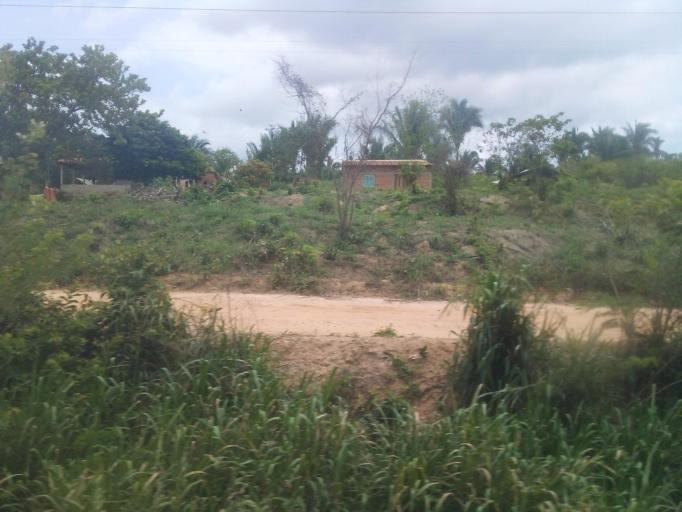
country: BR
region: Maranhao
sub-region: Santa Ines
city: Santa Ines
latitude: -3.6465
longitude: -45.7209
